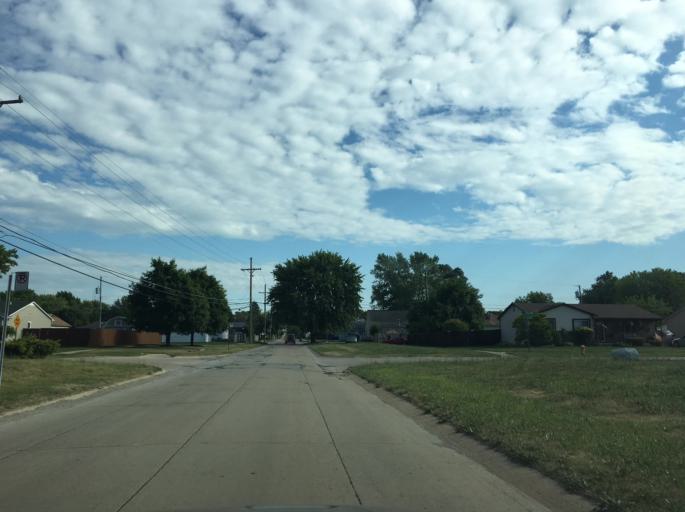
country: US
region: Michigan
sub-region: Macomb County
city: Fraser
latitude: 42.5455
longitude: -82.9104
